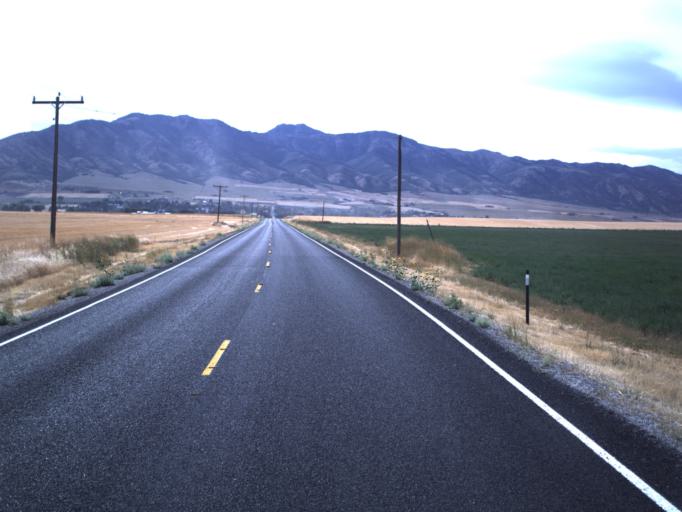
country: US
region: Utah
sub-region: Cache County
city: Benson
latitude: 41.9191
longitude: -112.0064
